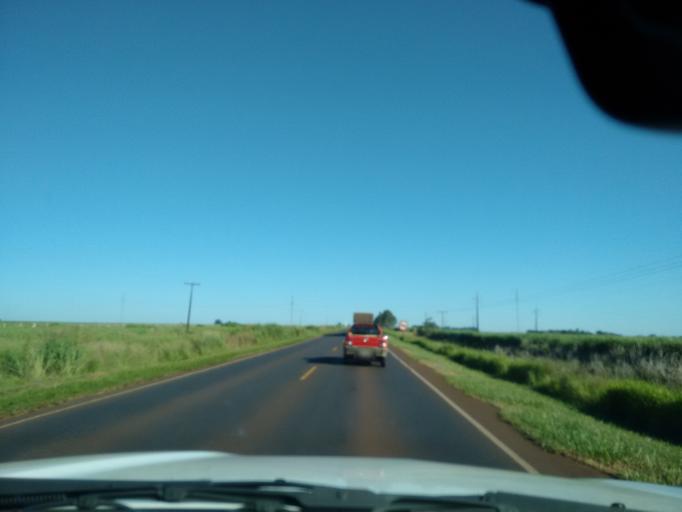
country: BR
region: Mato Grosso do Sul
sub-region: Dourados
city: Dourados
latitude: -22.3597
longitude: -54.8024
